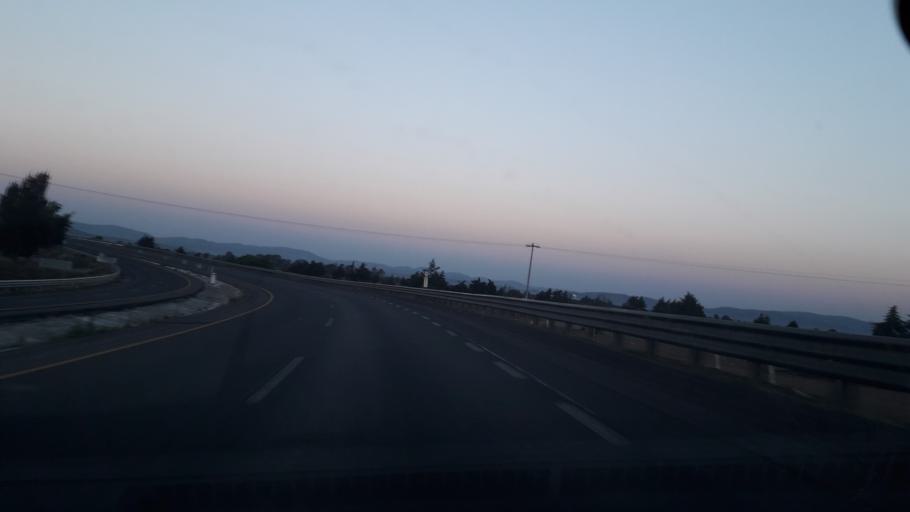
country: MX
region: Puebla
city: San Jose Esperanza
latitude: 18.8722
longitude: -97.3907
